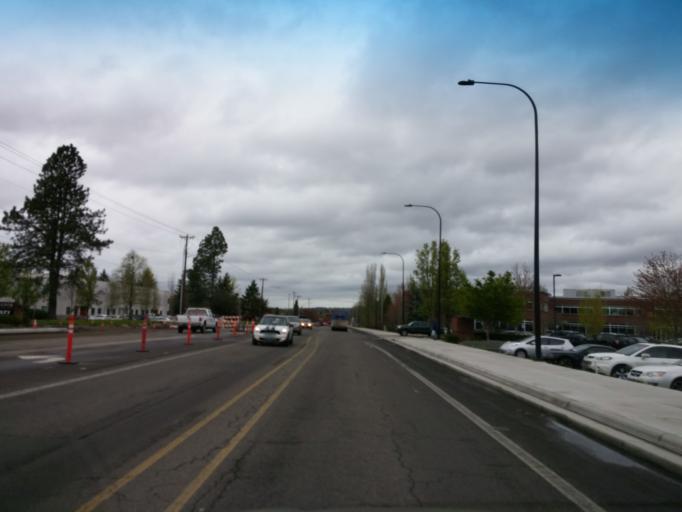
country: US
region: Oregon
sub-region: Washington County
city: Oak Hills
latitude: 45.5140
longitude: -122.8394
